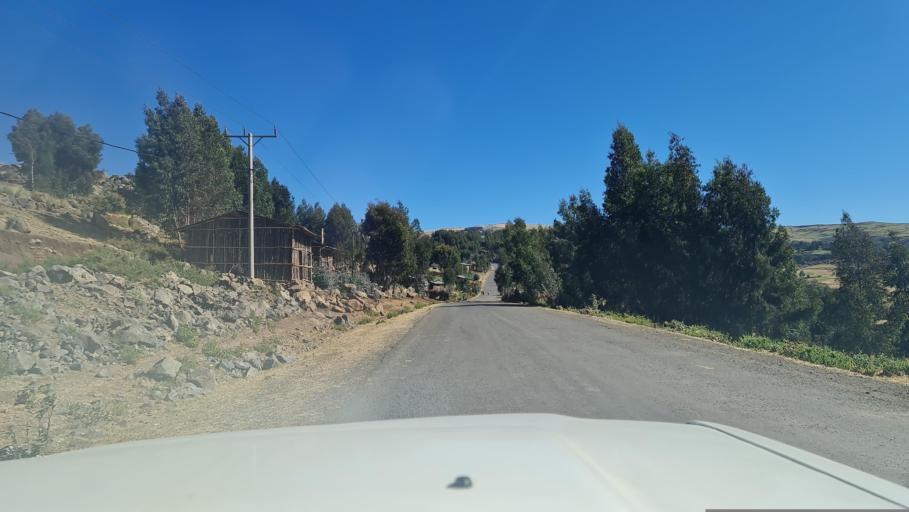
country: ET
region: Amhara
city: Debark'
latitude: 13.1047
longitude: 38.1455
